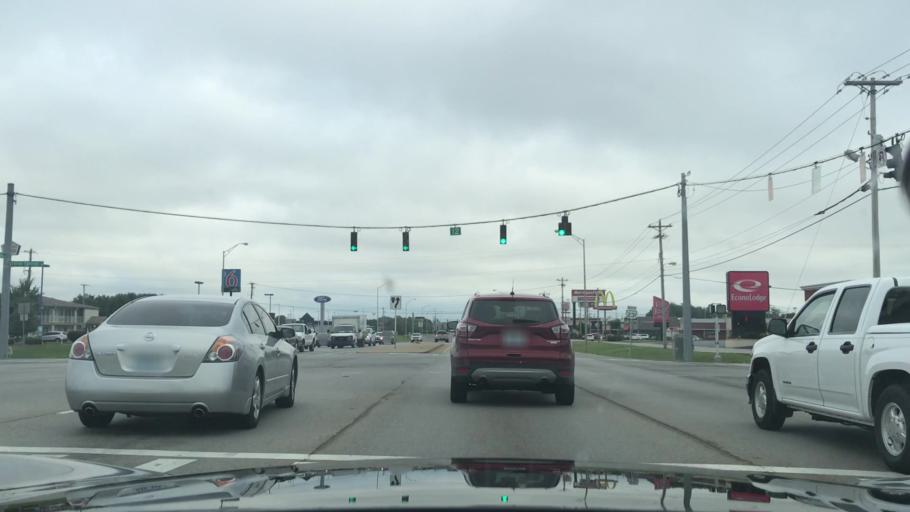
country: US
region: Kentucky
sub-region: Warren County
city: Bowling Green
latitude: 36.9400
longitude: -86.4206
